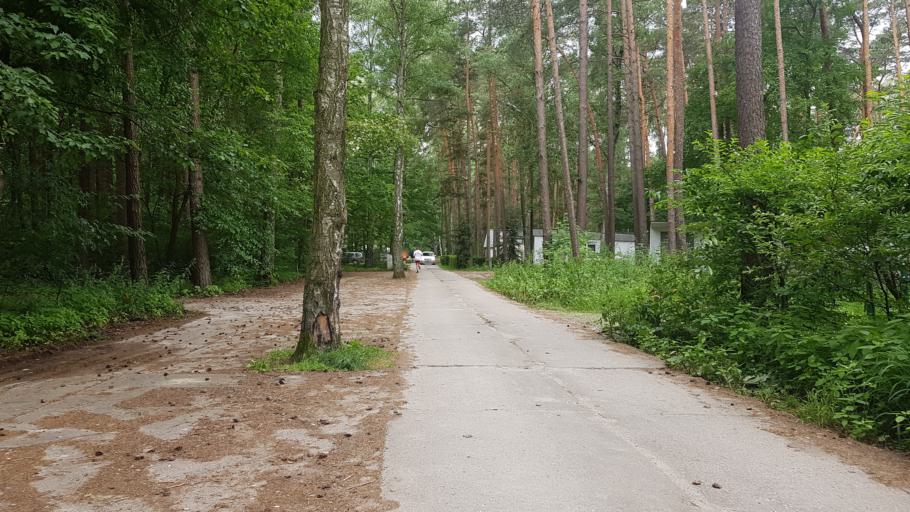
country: PL
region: Opole Voivodeship
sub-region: Powiat opolski
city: Chrzastowice
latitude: 50.7087
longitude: 18.1255
